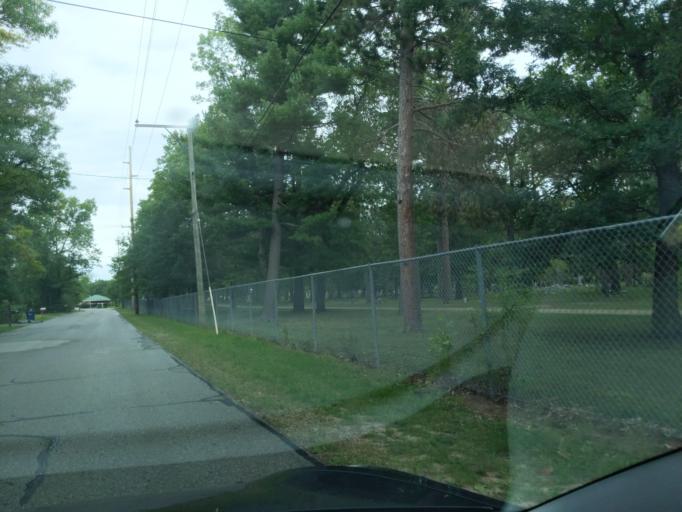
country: US
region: Michigan
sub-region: Grand Traverse County
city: Traverse City
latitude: 44.7561
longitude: -85.5903
